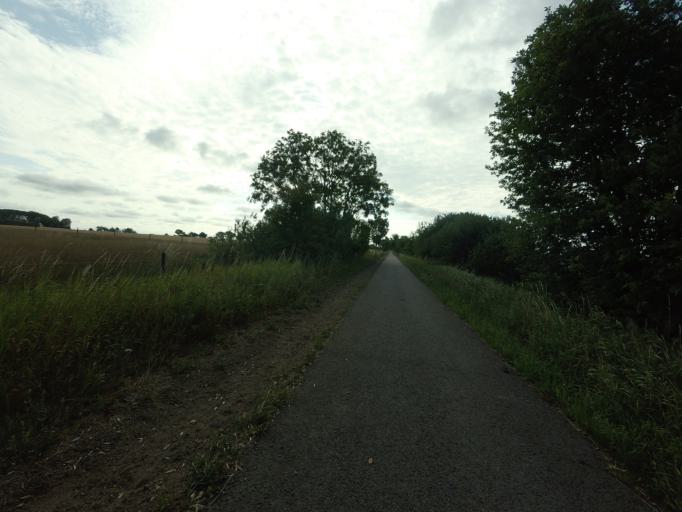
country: SE
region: Skane
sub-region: Hoganas Kommun
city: Hoganas
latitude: 56.1807
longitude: 12.6608
